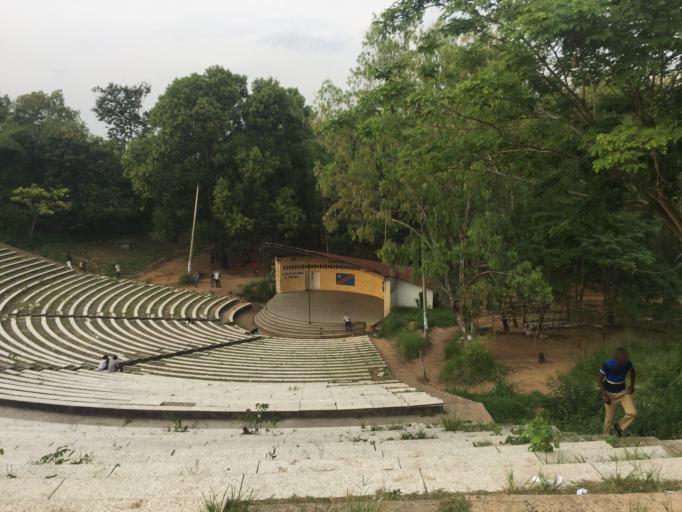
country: CD
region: Kinshasa
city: Masina
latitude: -4.4194
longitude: 15.3102
